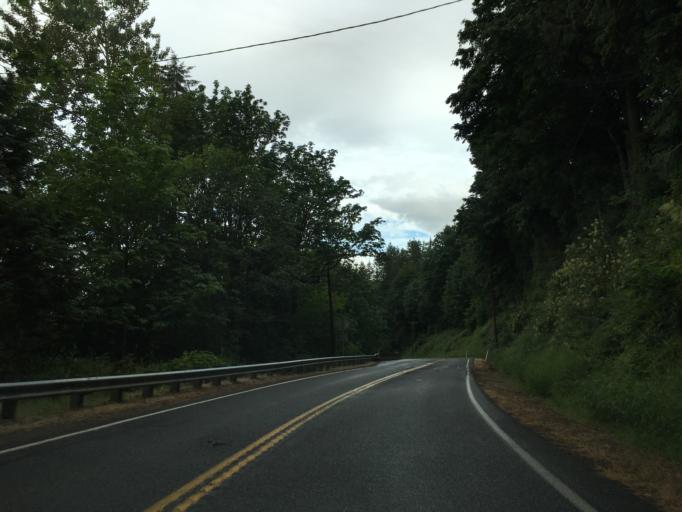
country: US
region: Washington
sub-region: Whatcom County
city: Sumas
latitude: 48.9645
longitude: -122.2256
